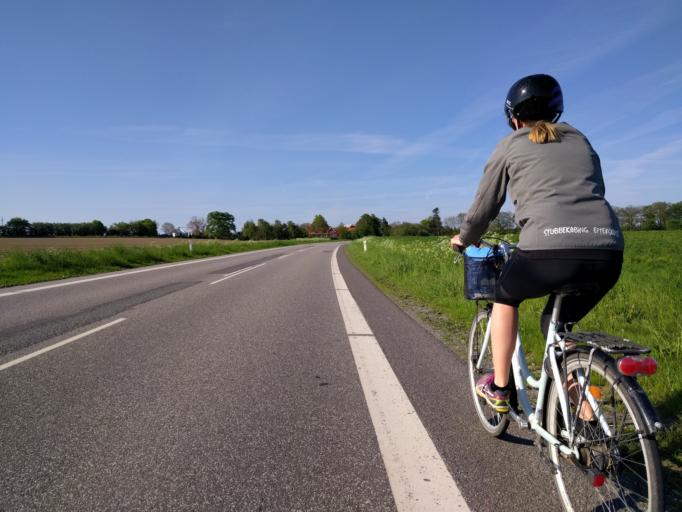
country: DK
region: Zealand
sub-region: Guldborgsund Kommune
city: Stubbekobing
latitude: 54.8496
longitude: 12.0139
